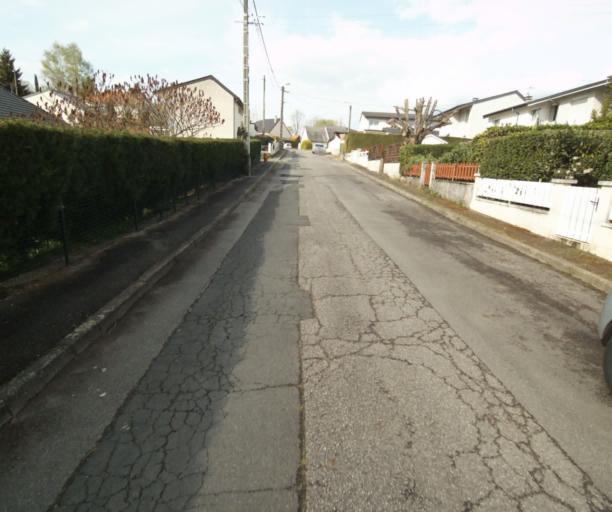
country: FR
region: Limousin
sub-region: Departement de la Correze
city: Tulle
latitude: 45.2582
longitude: 1.7394
